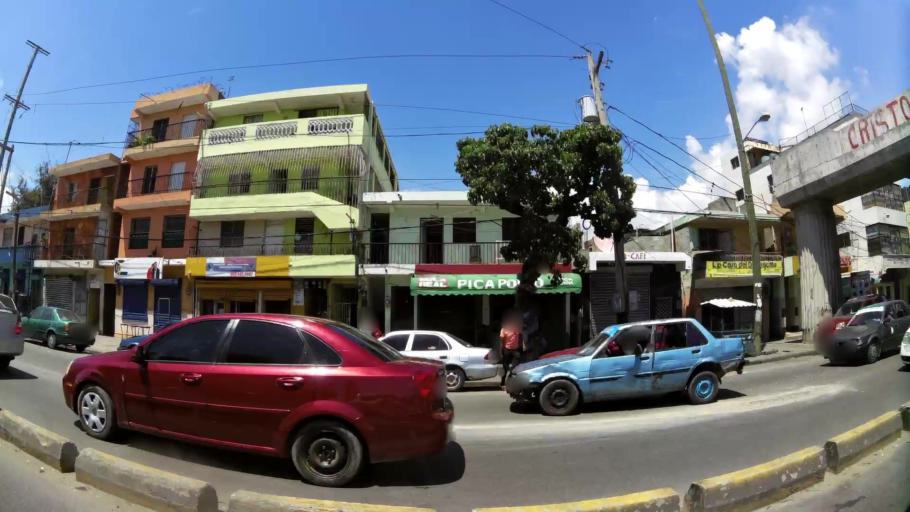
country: DO
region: Nacional
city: Ensanche Luperon
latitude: 18.4997
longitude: -69.8904
